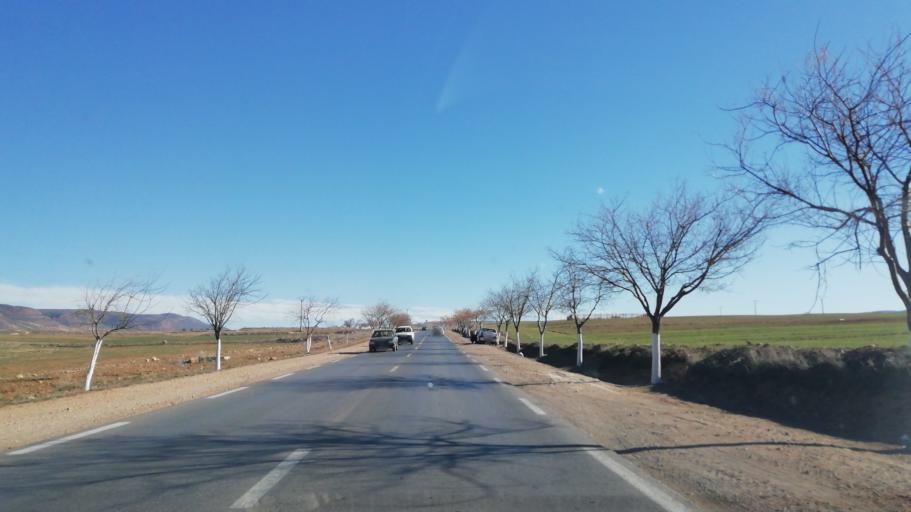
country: DZ
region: Tlemcen
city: Sebdou
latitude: 34.6566
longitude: -1.3034
